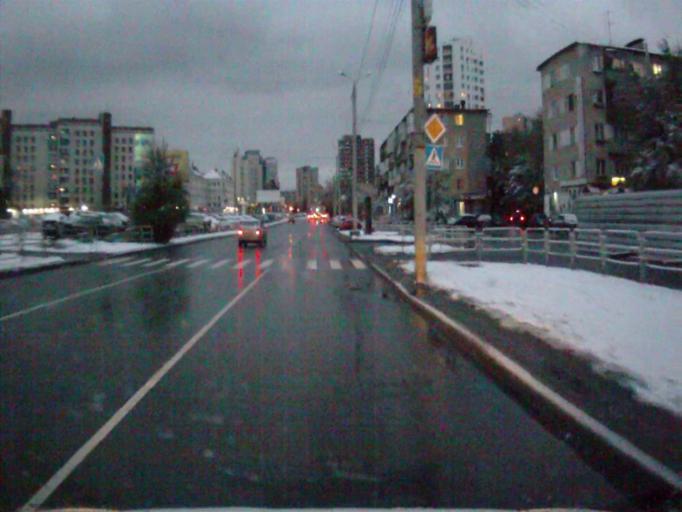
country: RU
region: Chelyabinsk
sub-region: Gorod Chelyabinsk
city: Chelyabinsk
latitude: 55.1486
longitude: 61.3931
